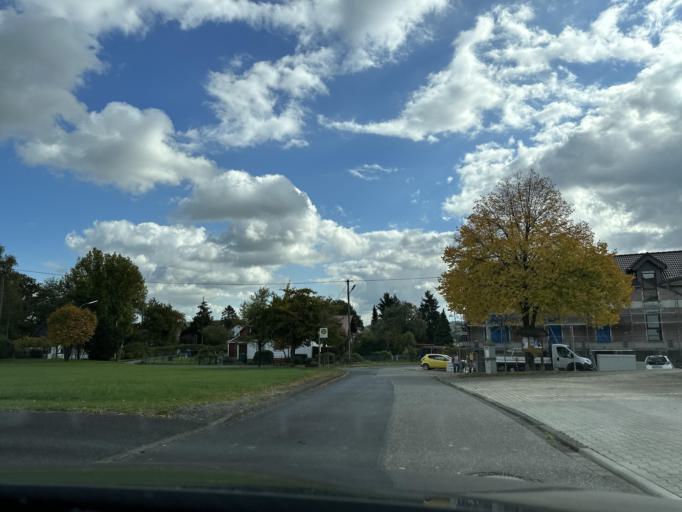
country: DE
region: Rheinland-Pfalz
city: Kescheid
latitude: 50.6619
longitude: 7.4723
